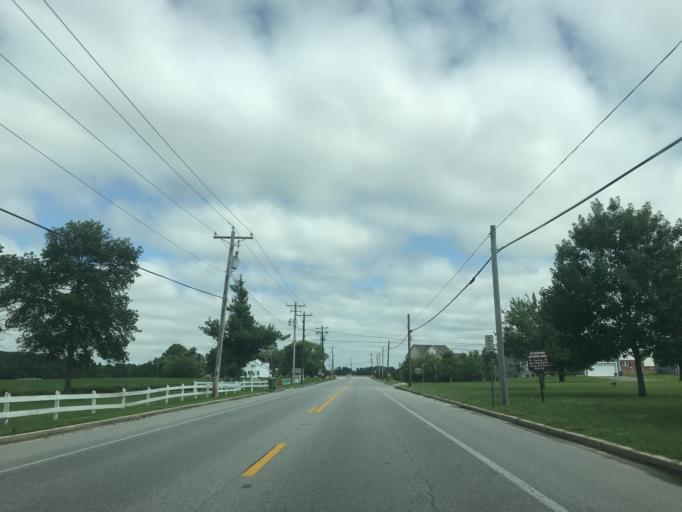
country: US
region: Maryland
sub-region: Caroline County
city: Ridgely
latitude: 38.9521
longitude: -75.8858
